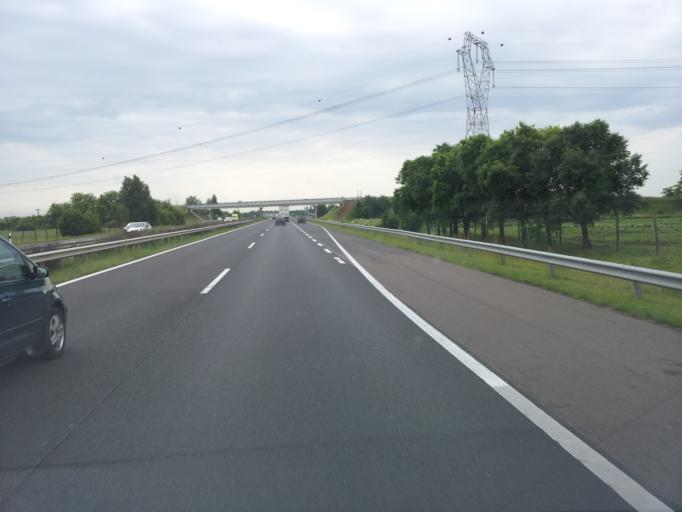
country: HU
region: Heves
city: Adacs
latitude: 47.7168
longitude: 19.9976
